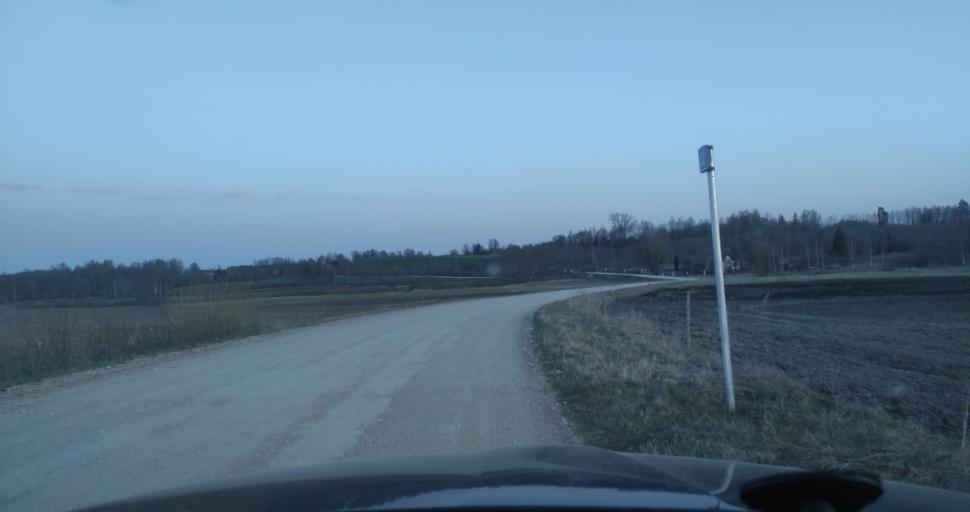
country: LV
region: Aizpute
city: Aizpute
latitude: 56.6513
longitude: 21.7956
